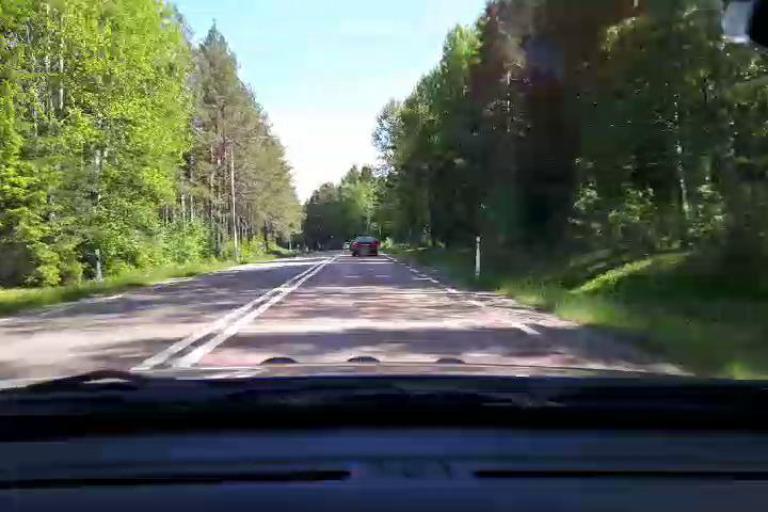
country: SE
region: Gaevleborg
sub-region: Hudiksvalls Kommun
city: Delsbo
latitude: 61.7995
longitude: 16.4948
